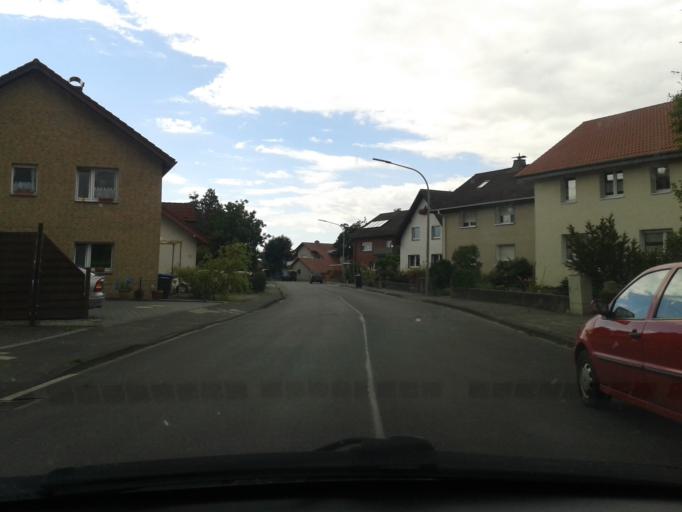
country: DE
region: North Rhine-Westphalia
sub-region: Regierungsbezirk Detmold
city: Paderborn
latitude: 51.7347
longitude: 8.6760
